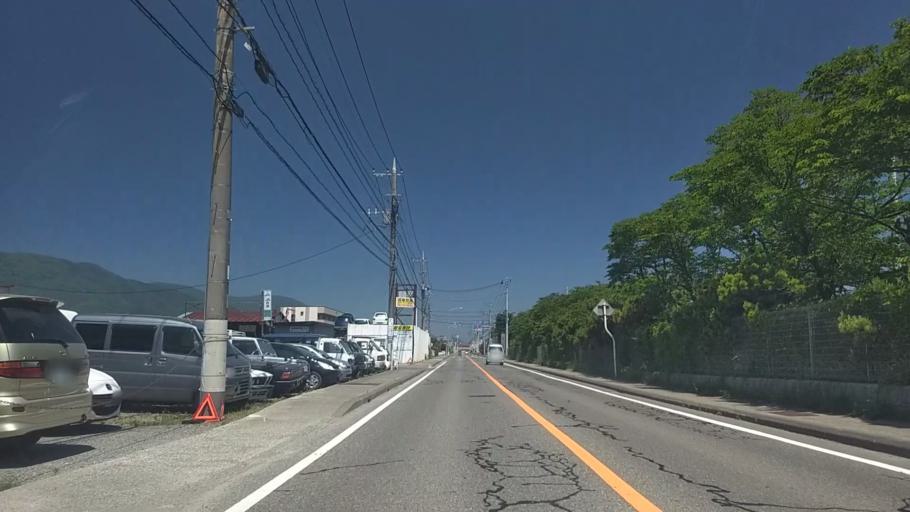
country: JP
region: Yamanashi
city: Nirasaki
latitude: 35.6918
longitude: 138.4602
